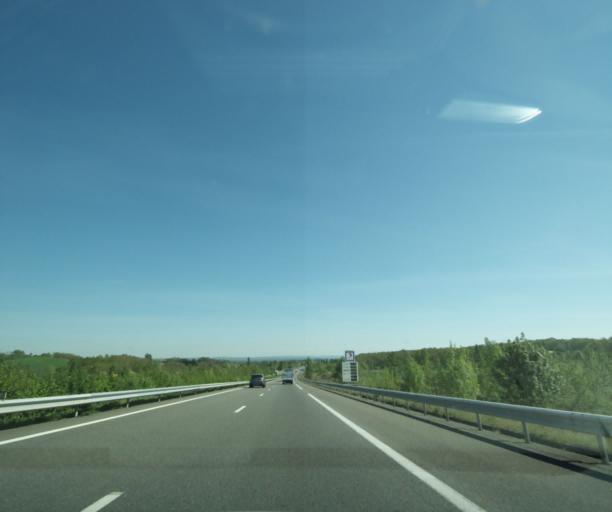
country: FR
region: Midi-Pyrenees
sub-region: Departement du Tarn-et-Garonne
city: Caussade
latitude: 44.2425
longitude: 1.5192
